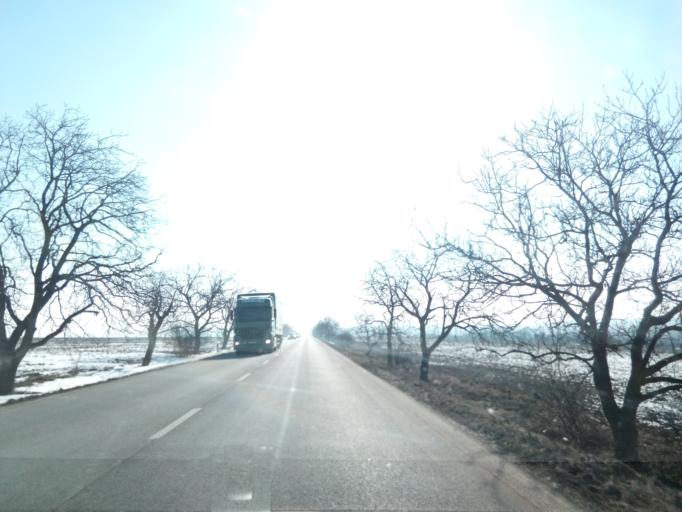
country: SK
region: Kosicky
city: Secovce
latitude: 48.7119
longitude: 21.6178
